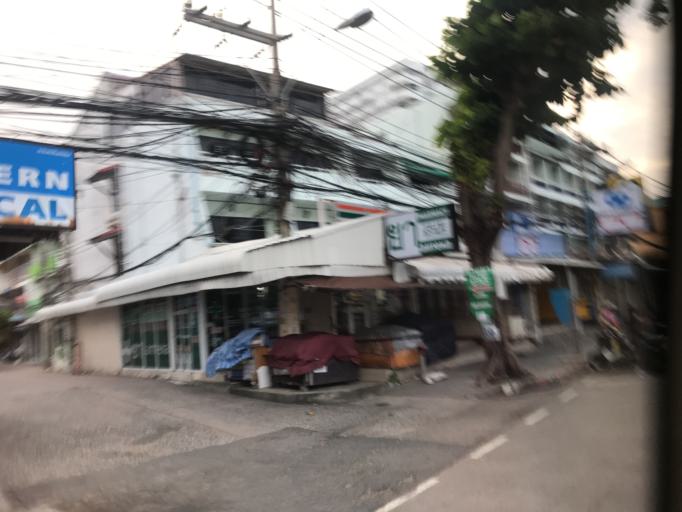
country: TH
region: Chon Buri
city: Phatthaya
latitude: 12.8962
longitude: 100.8694
